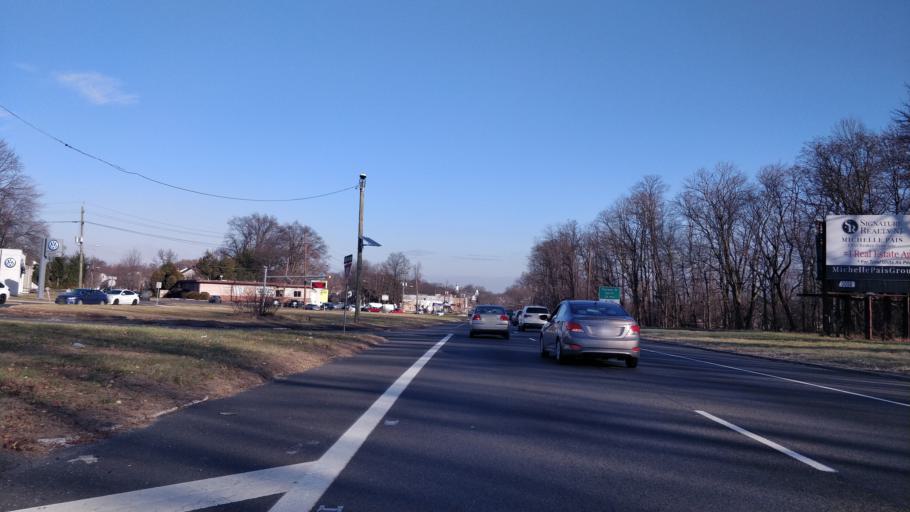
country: US
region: New Jersey
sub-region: Union County
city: Kenilworth
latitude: 40.6914
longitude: -74.2844
